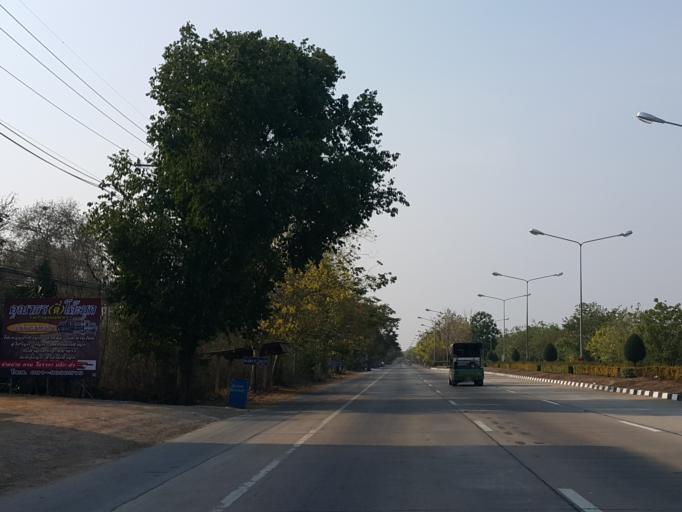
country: TH
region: Suphan Buri
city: Sam Chuk
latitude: 14.7718
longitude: 100.0914
